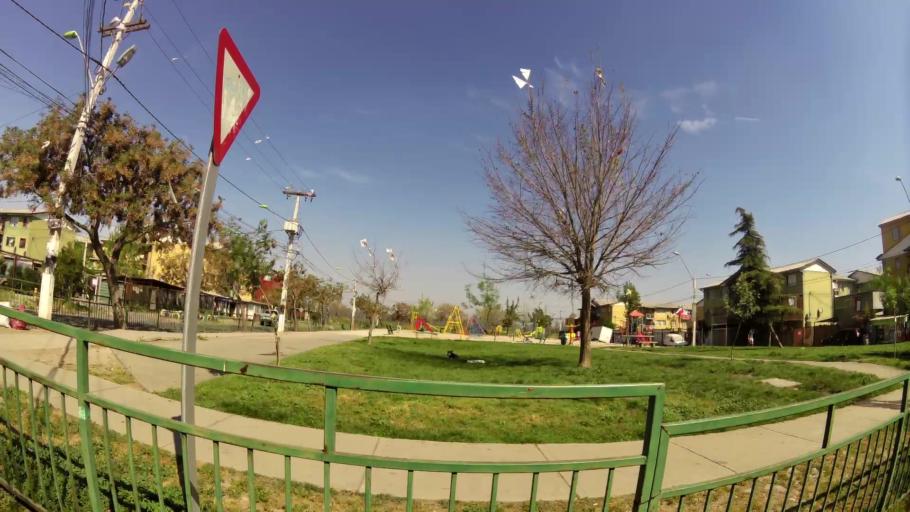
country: CL
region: Santiago Metropolitan
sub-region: Provincia de Santiago
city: La Pintana
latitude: -33.5646
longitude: -70.6247
